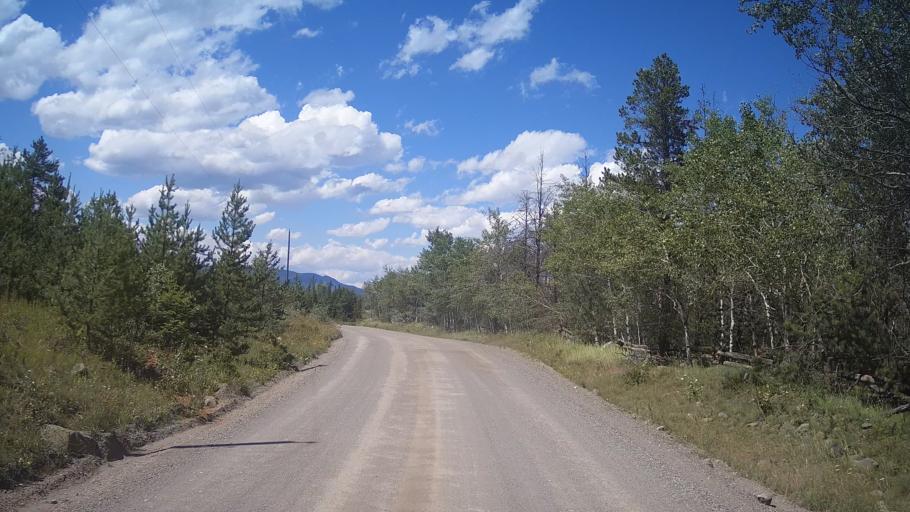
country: CA
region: British Columbia
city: Cache Creek
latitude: 51.2497
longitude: -121.6650
